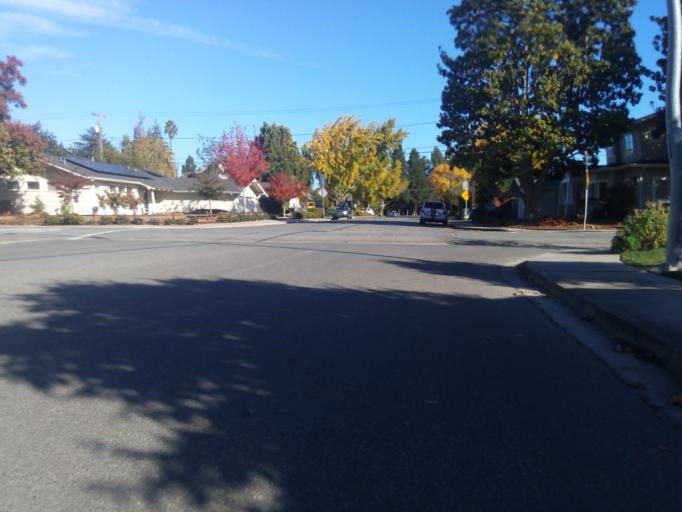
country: US
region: California
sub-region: Santa Clara County
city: Mountain View
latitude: 37.3771
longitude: -122.0798
